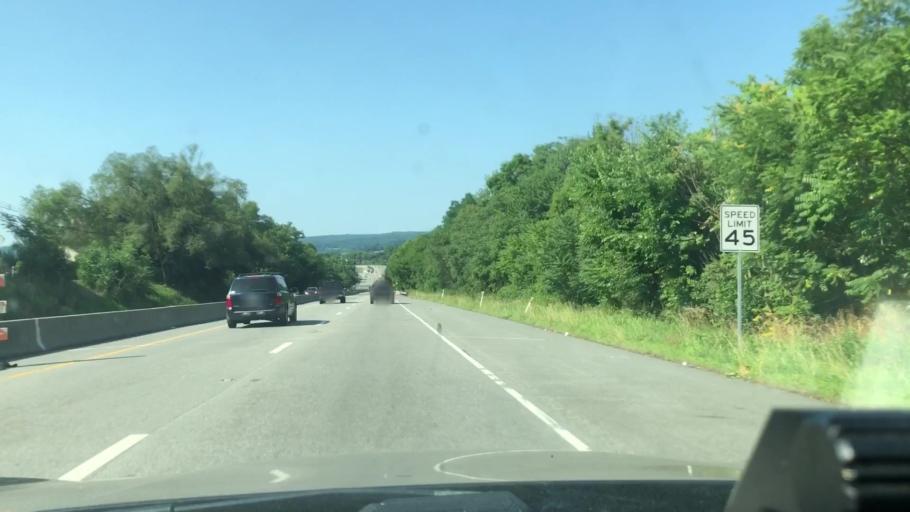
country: US
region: Pennsylvania
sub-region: Montgomery County
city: Pottstown
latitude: 40.2595
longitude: -75.6550
